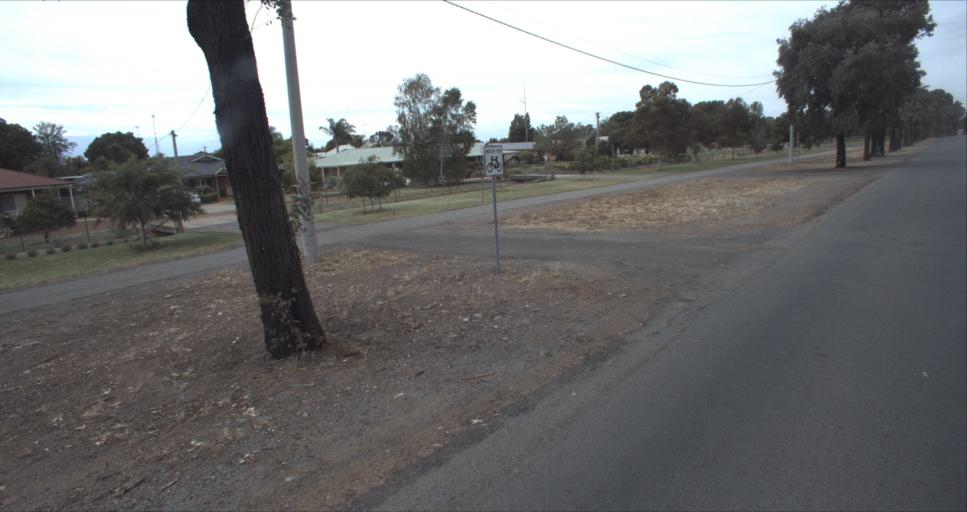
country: AU
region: New South Wales
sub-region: Leeton
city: Leeton
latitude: -34.5458
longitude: 146.4108
